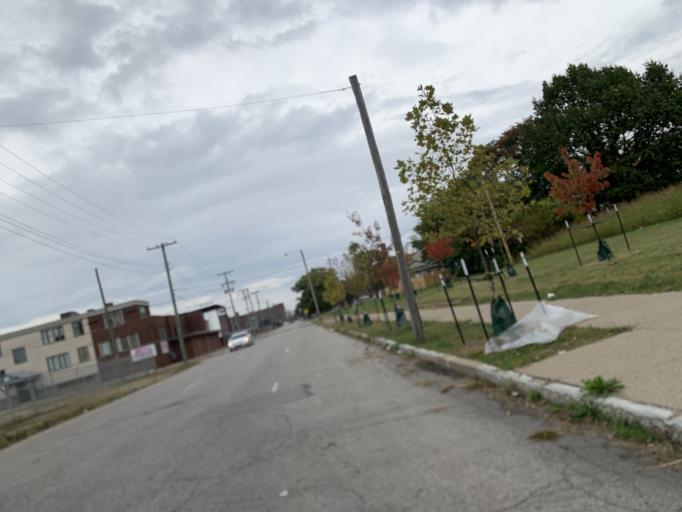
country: US
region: Kentucky
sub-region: Jefferson County
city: Louisville
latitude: 38.2380
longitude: -85.7665
